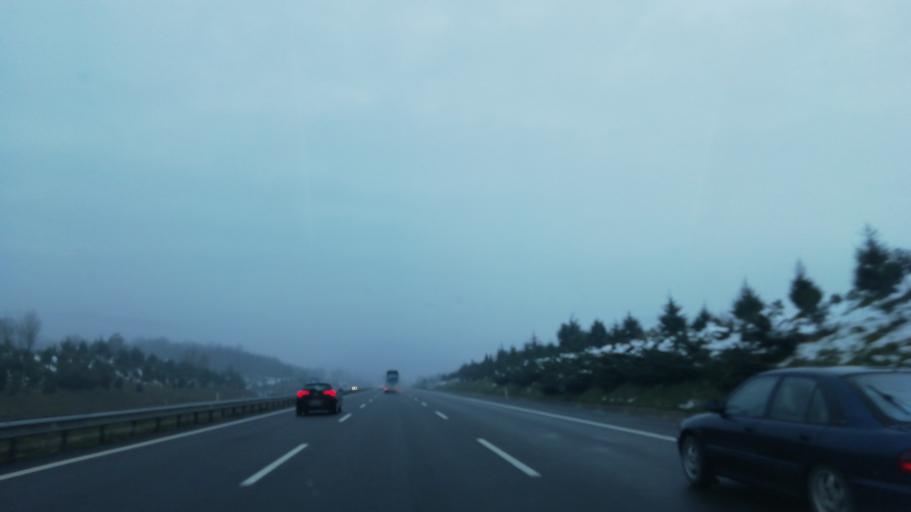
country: TR
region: Duzce
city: Kaynasli
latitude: 40.7799
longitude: 31.3447
